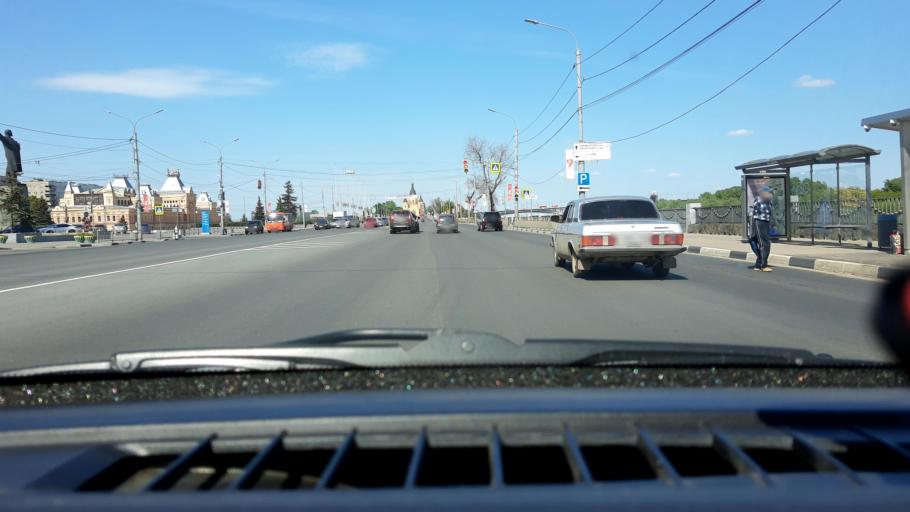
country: RU
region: Nizjnij Novgorod
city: Nizhniy Novgorod
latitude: 56.3242
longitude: 43.9617
